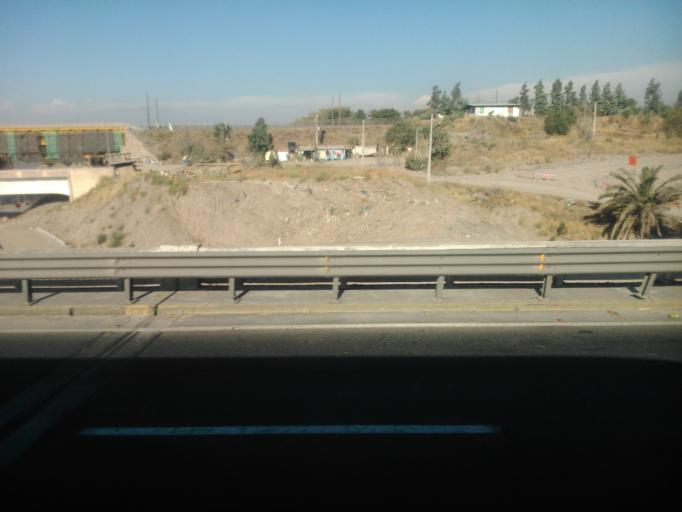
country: CL
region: Santiago Metropolitan
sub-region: Provincia de Maipo
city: Buin
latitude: -33.6920
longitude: -70.7232
